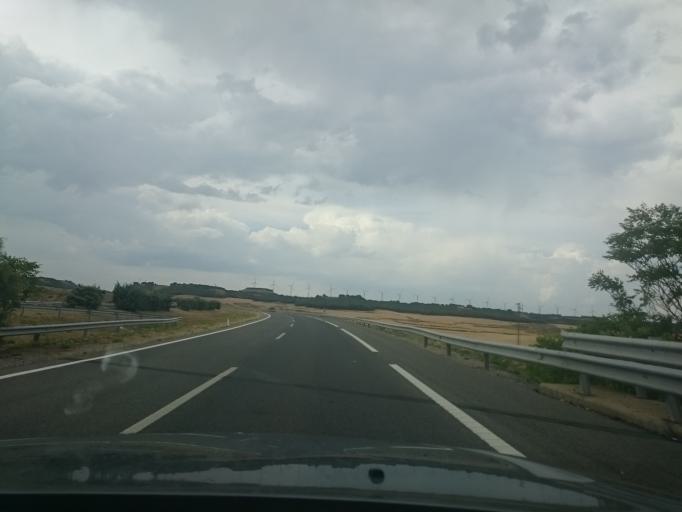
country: ES
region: Navarre
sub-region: Provincia de Navarra
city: Murchante
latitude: 42.0711
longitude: -1.6919
